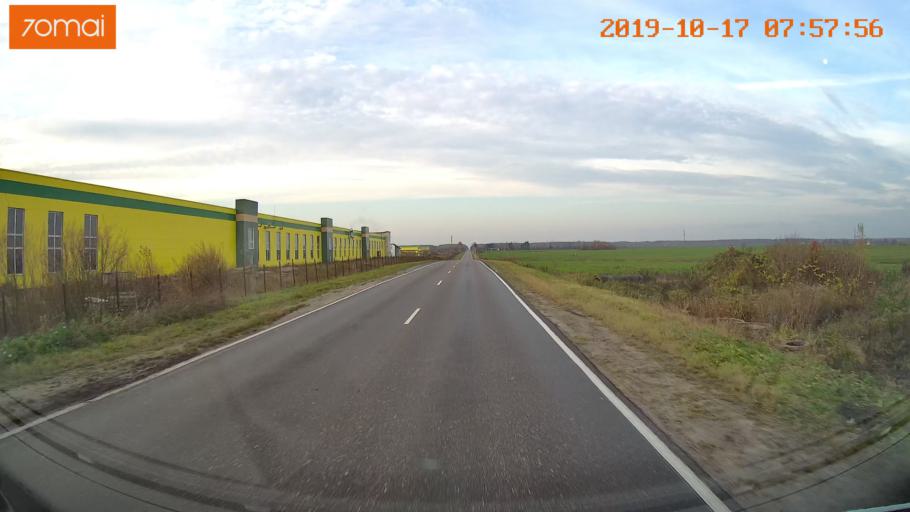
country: RU
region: Vladimir
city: Bavleny
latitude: 56.4074
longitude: 39.5674
